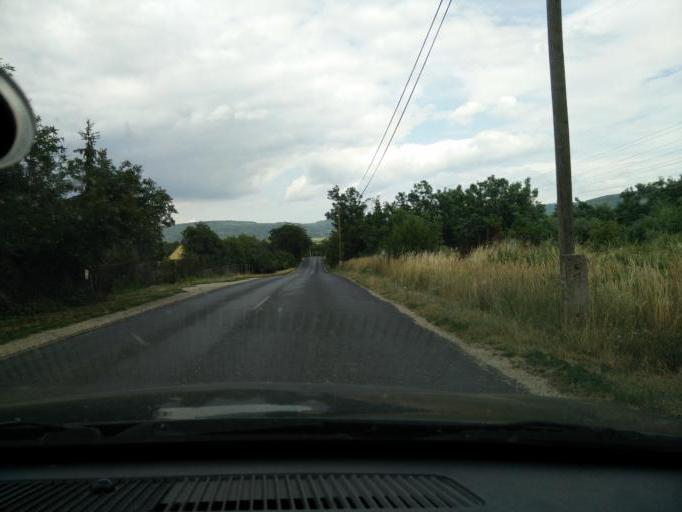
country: HU
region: Komarom-Esztergom
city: Baj
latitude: 47.6609
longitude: 18.3522
